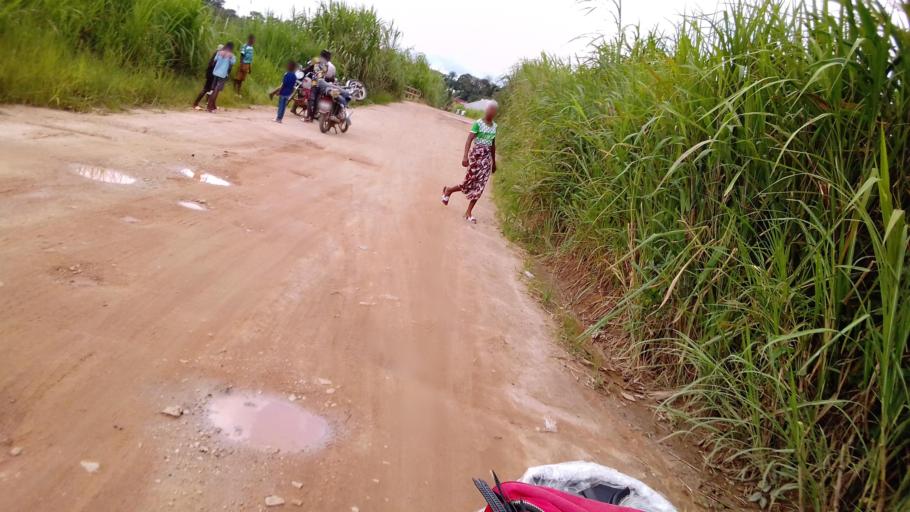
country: SL
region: Eastern Province
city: Koidu
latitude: 8.6720
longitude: -10.9802
